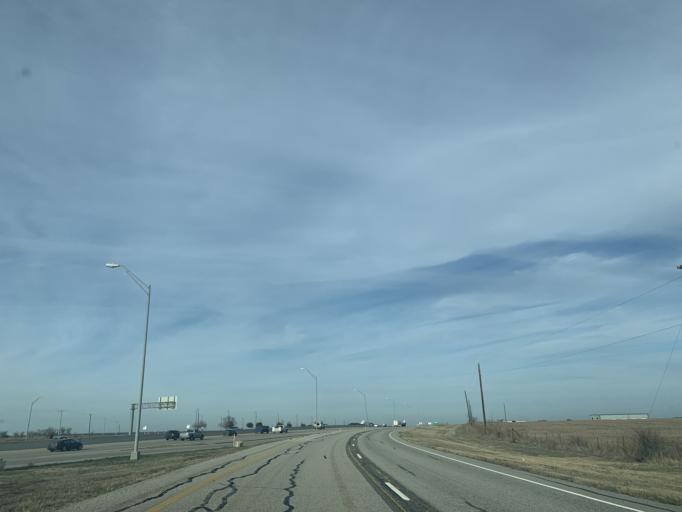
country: US
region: Texas
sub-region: Bell County
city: Salado
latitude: 30.9064
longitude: -97.5559
